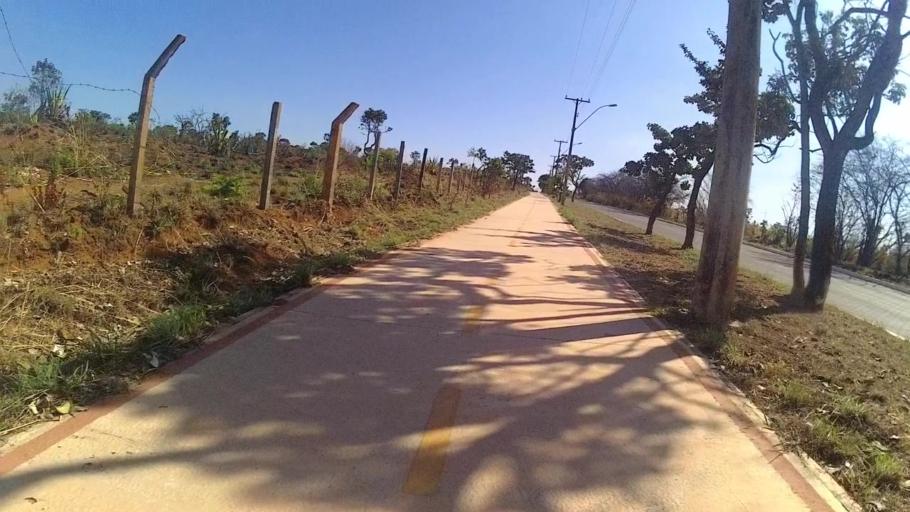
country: BR
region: Federal District
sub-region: Brasilia
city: Brasilia
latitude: -15.6528
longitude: -47.8942
